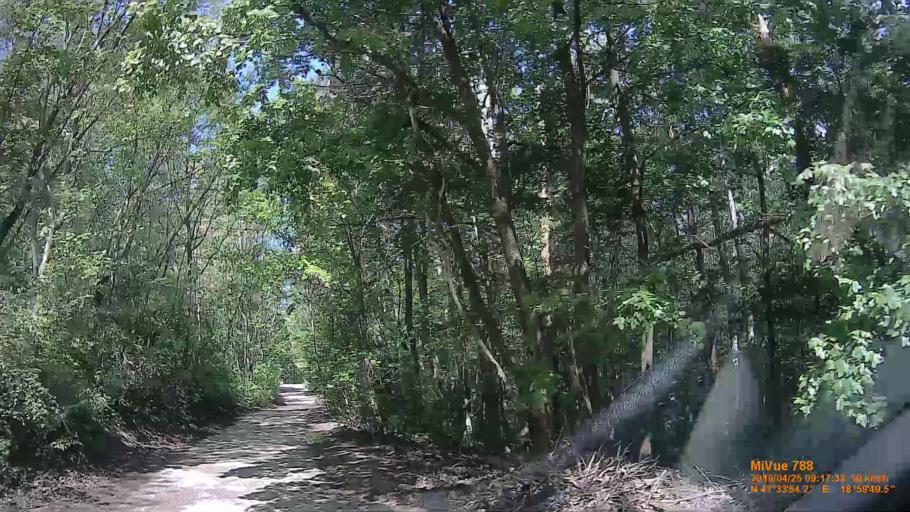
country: HU
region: Pest
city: Urom
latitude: 47.5651
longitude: 18.9970
